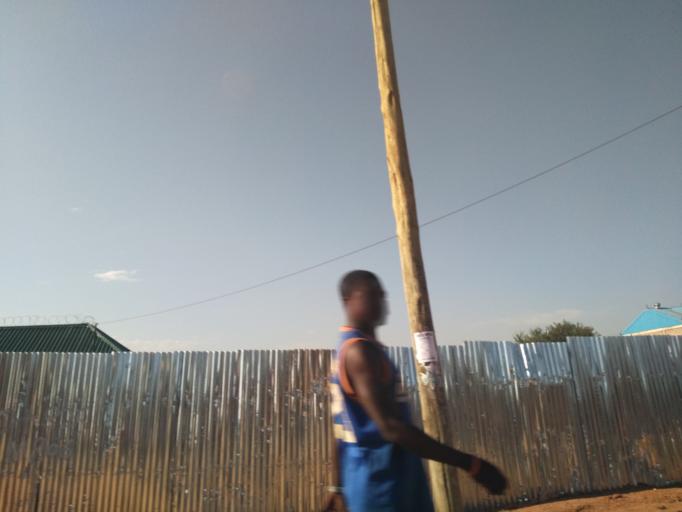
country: TZ
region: Mwanza
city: Mwanza
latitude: -2.5065
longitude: 32.8939
